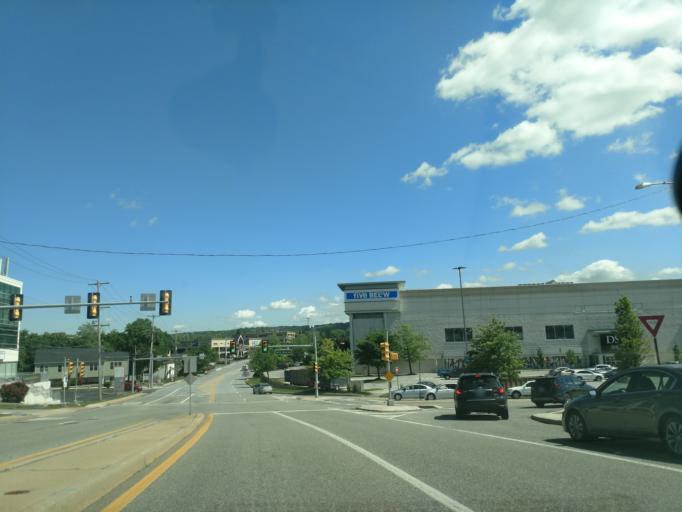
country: US
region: Pennsylvania
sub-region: Montgomery County
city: King of Prussia
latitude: 40.0913
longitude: -75.3849
